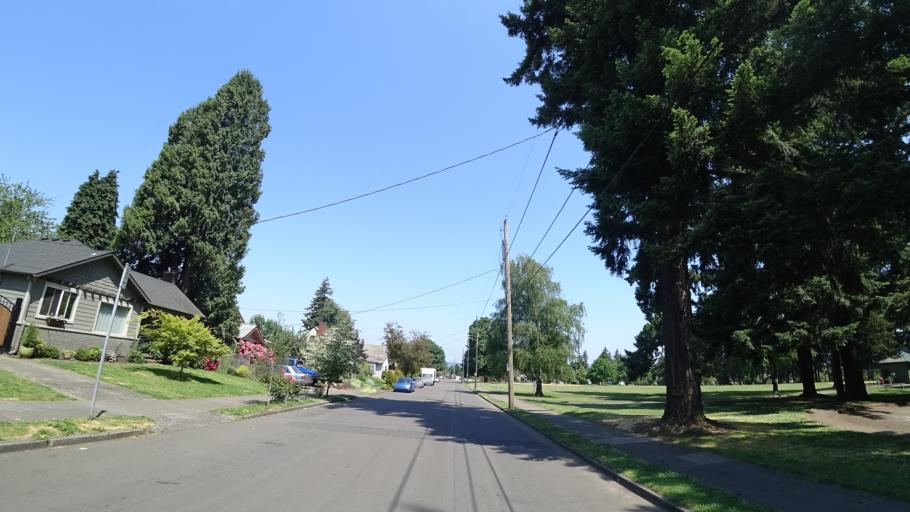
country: US
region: Oregon
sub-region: Multnomah County
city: Portland
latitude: 45.5647
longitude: -122.6460
